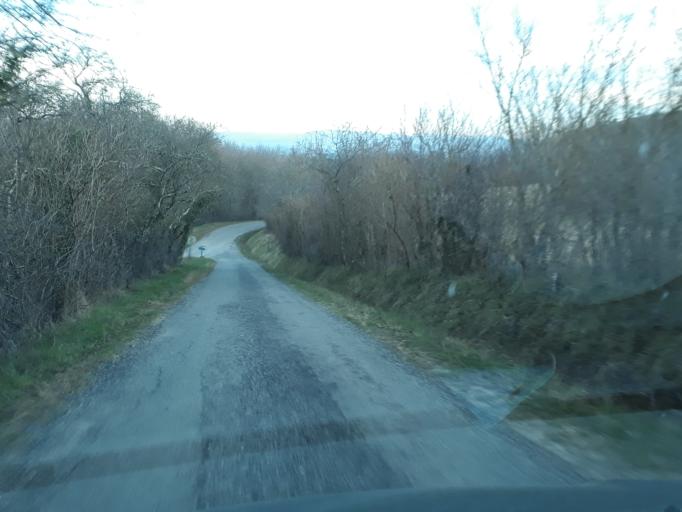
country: FR
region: Midi-Pyrenees
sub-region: Departement de la Haute-Garonne
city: Montesquieu-Volvestre
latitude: 43.1754
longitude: 1.3209
